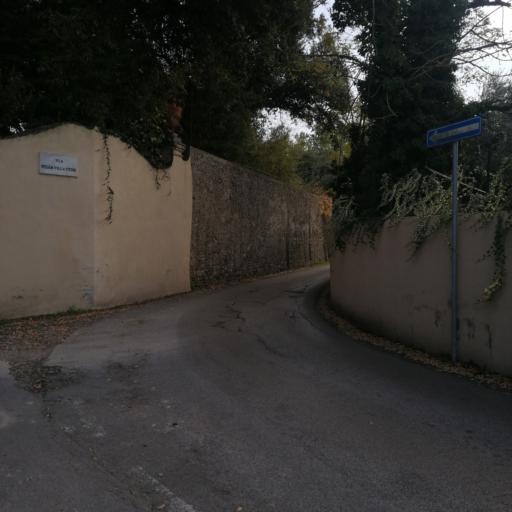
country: IT
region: Tuscany
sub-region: Province of Florence
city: Bagno a Ripoli
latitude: 43.7594
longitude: 11.3175
